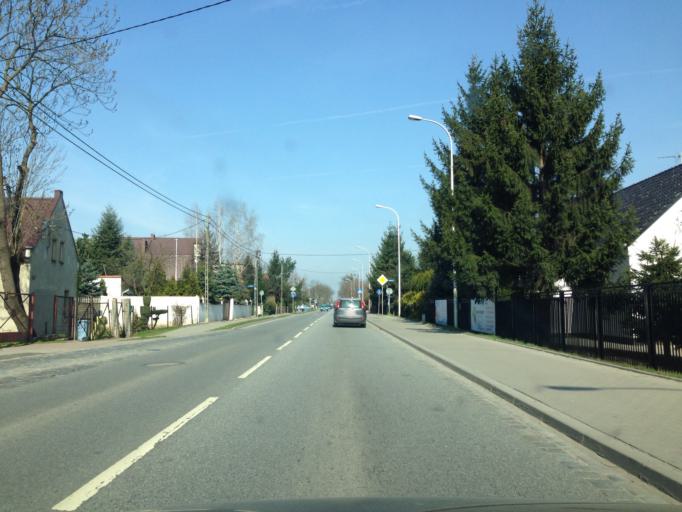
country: PL
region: Lower Silesian Voivodeship
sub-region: Powiat wroclawski
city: Kamieniec Wroclawski
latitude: 51.0974
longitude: 17.1636
